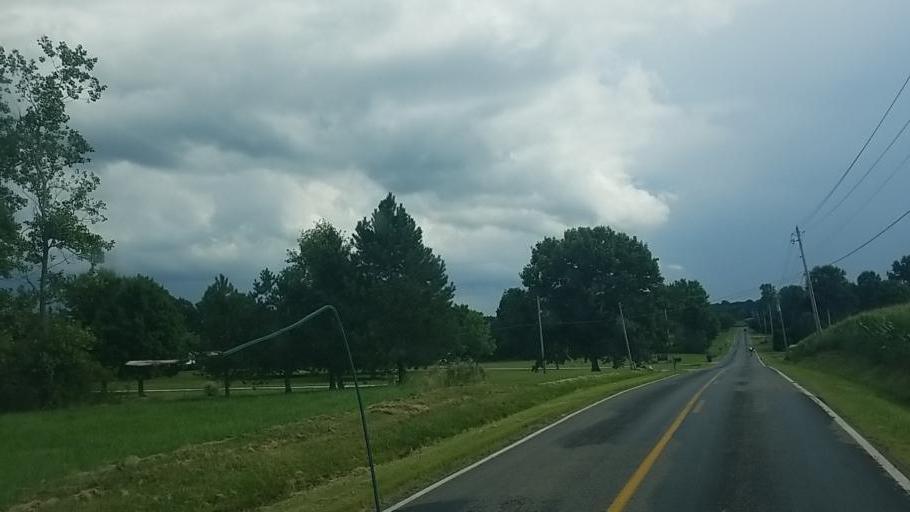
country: US
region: Ohio
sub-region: Wayne County
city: Creston
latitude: 41.0080
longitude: -81.9110
